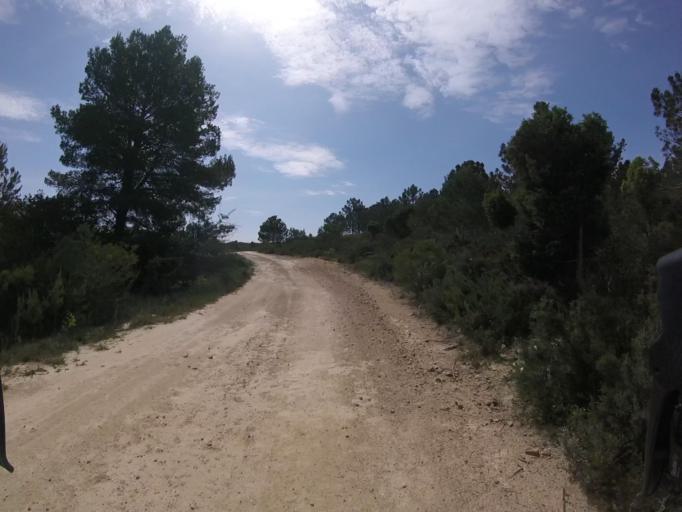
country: ES
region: Valencia
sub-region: Provincia de Castello
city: Cuevas de Vinroma
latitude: 40.2831
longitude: 0.1229
